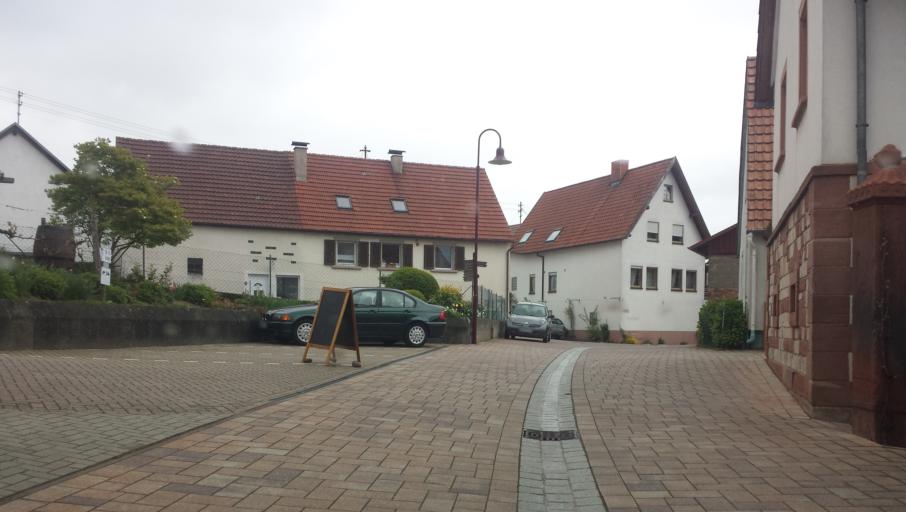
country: DE
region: Rheinland-Pfalz
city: Schweigen-Rechtenbach
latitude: 49.0523
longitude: 7.9522
